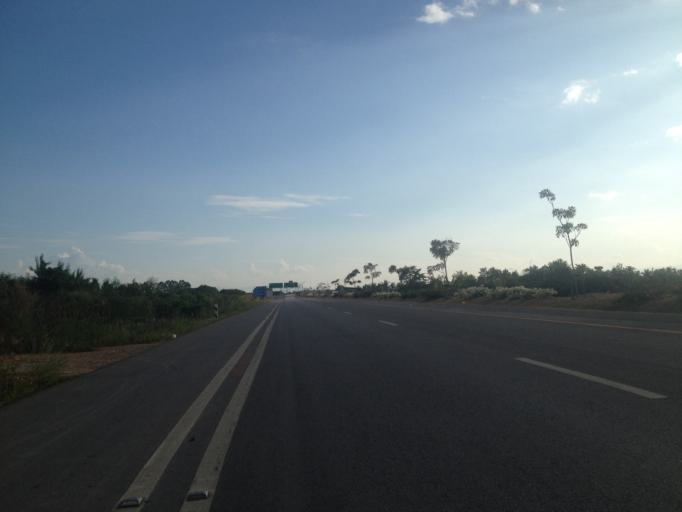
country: TH
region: Chiang Mai
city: San Pa Tong
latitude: 18.6160
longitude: 98.8367
